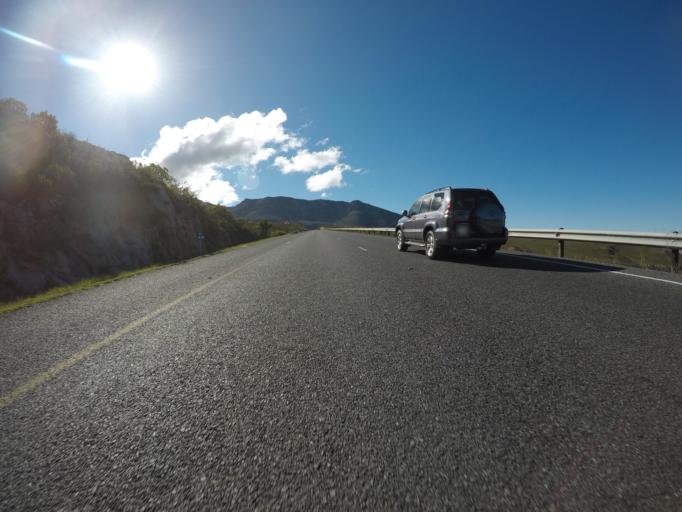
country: ZA
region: Western Cape
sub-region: Overberg District Municipality
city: Grabouw
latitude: -34.2218
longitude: 19.1723
